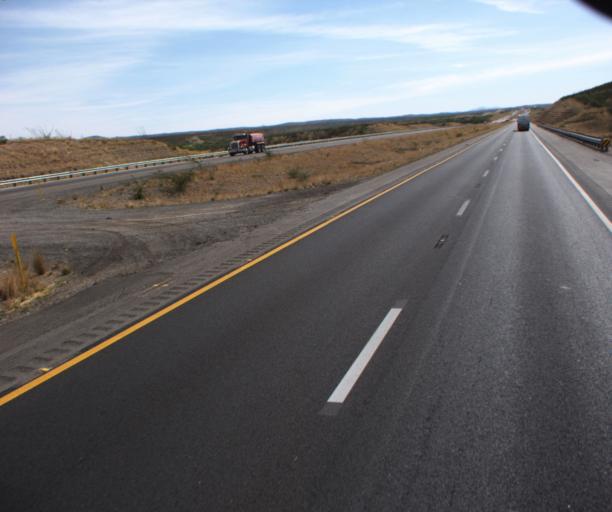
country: US
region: Arizona
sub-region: Cochise County
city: Mescal
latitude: 31.9868
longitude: -110.5778
